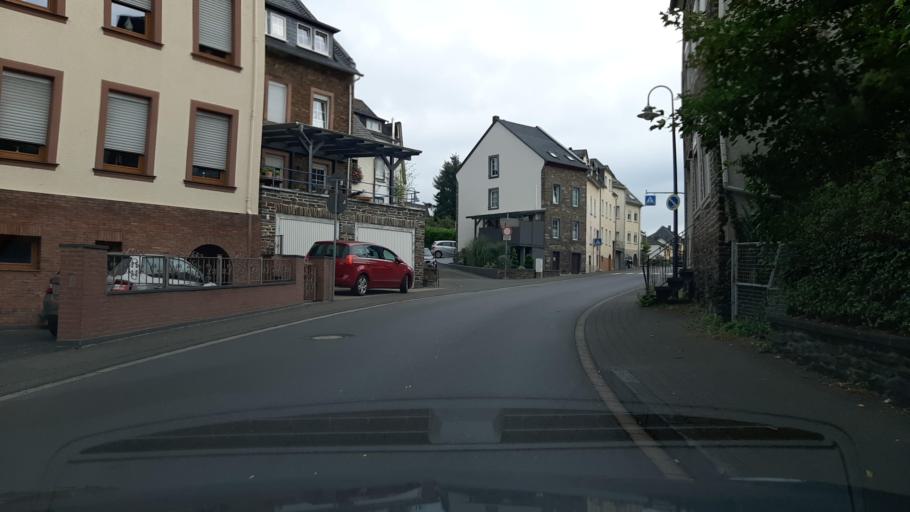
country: DE
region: Rheinland-Pfalz
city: Traben-Trarbach
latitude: 49.9527
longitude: 7.1200
